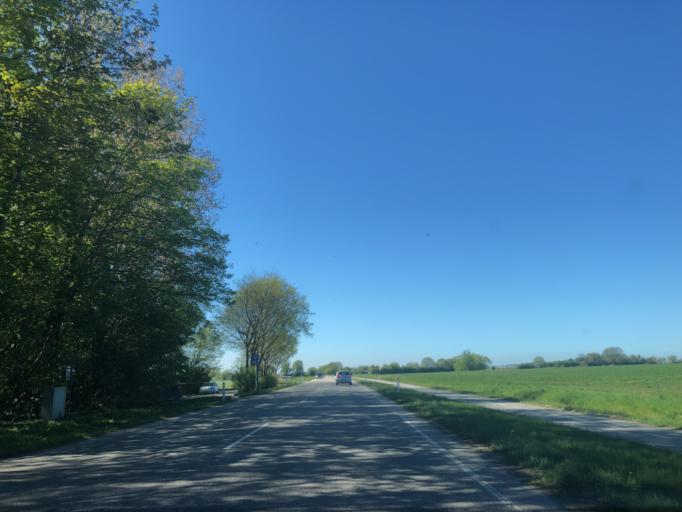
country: DK
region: Zealand
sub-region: Stevns Kommune
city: Harlev
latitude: 55.3585
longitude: 12.3141
